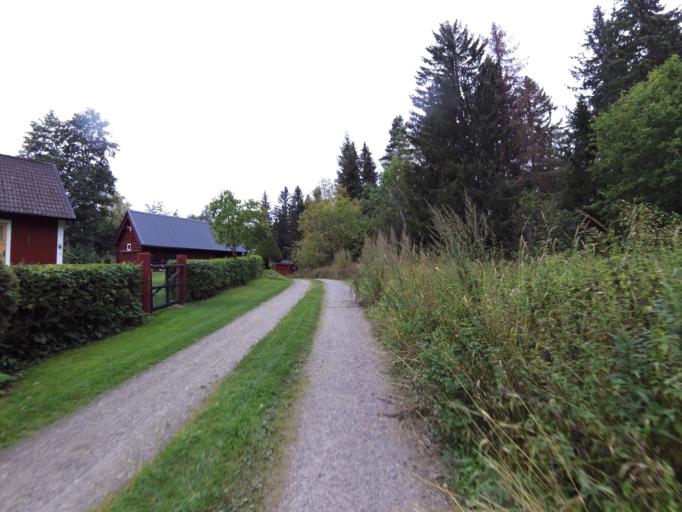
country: SE
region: Gaevleborg
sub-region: Gavle Kommun
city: Valbo
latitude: 60.7543
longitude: 16.9707
